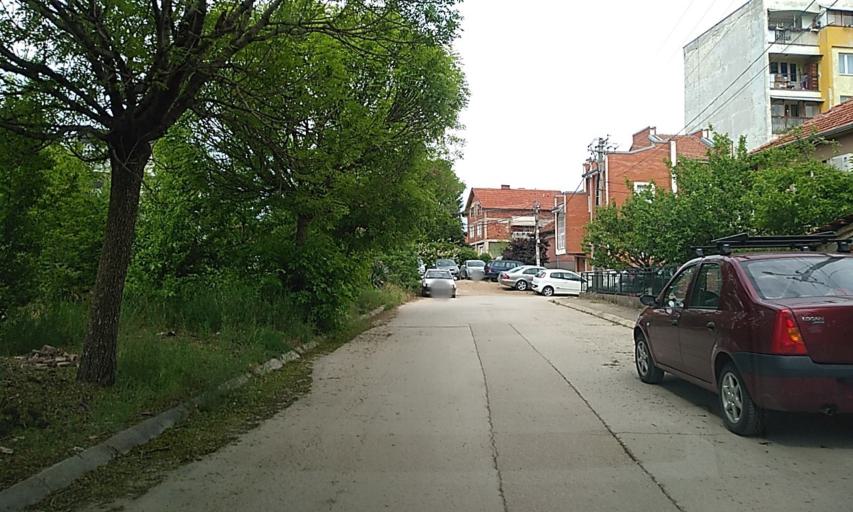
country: RS
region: Central Serbia
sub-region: Nisavski Okrug
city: Nis
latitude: 43.3361
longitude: 21.9088
